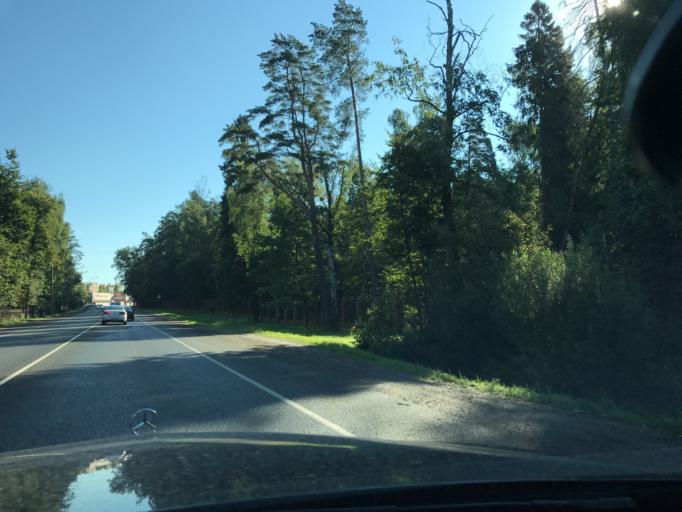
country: RU
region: Moskovskaya
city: Sverdlovskiy
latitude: 55.9179
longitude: 38.1215
